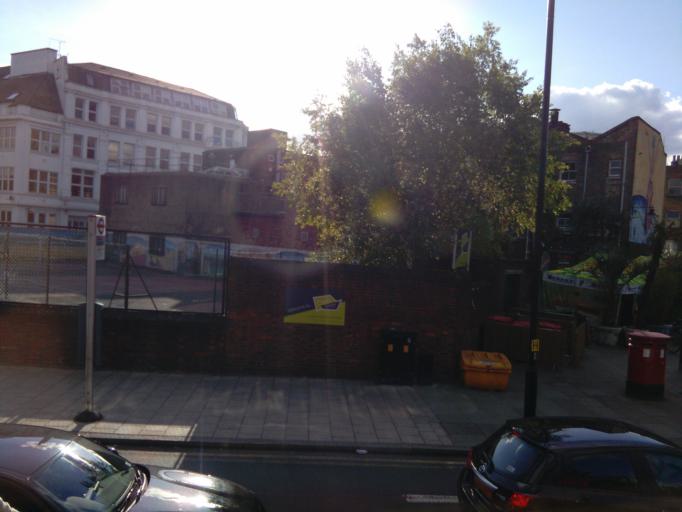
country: GB
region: England
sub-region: Greater London
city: Lambeth
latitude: 51.5016
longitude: -0.1108
